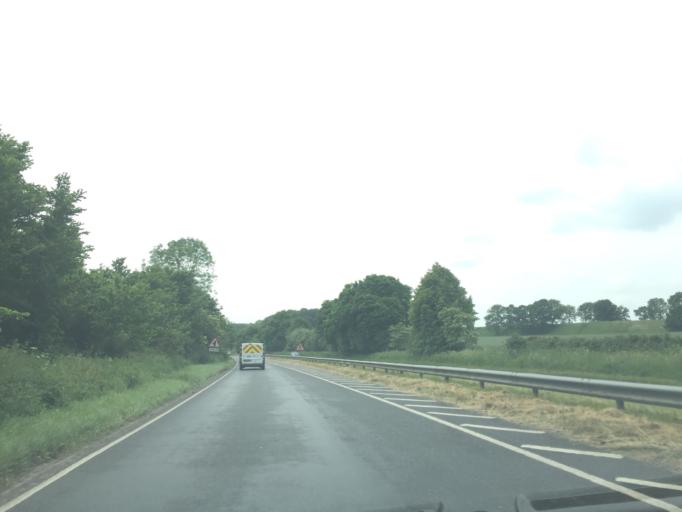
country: GB
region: England
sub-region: Hampshire
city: Four Marks
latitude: 51.0999
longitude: -1.0739
